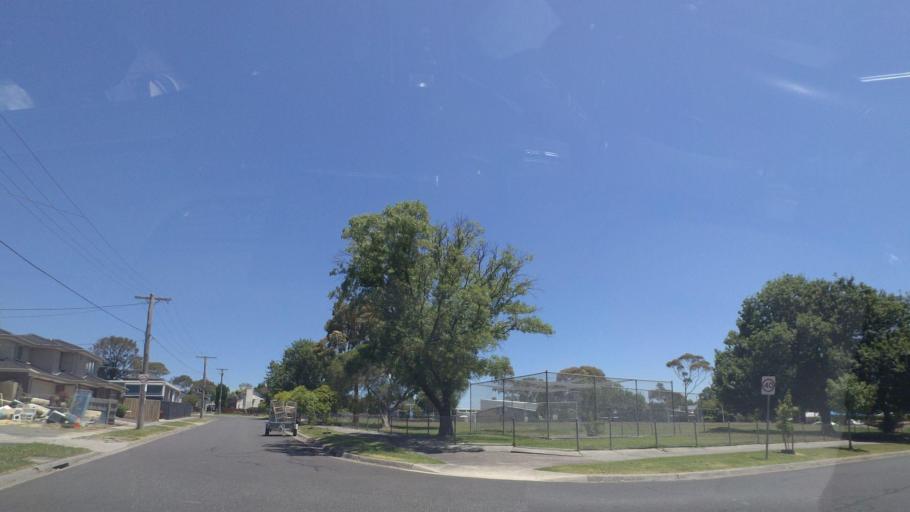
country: AU
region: Victoria
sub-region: Knox
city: Boronia
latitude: -37.8694
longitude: 145.2669
